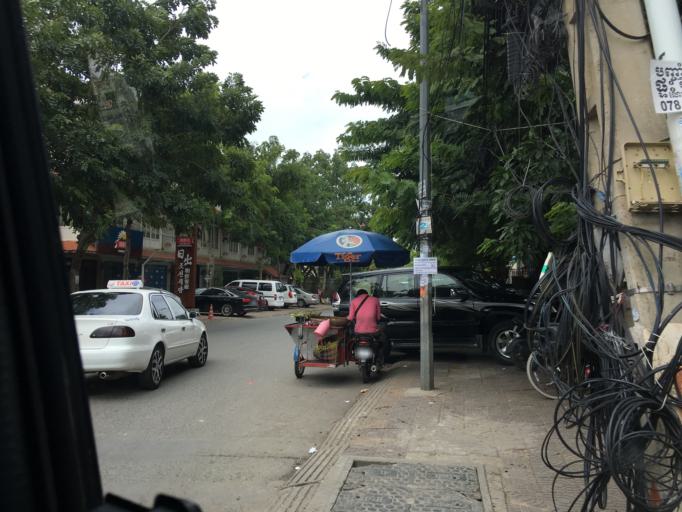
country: KH
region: Phnom Penh
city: Phnom Penh
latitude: 11.5382
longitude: 104.9234
